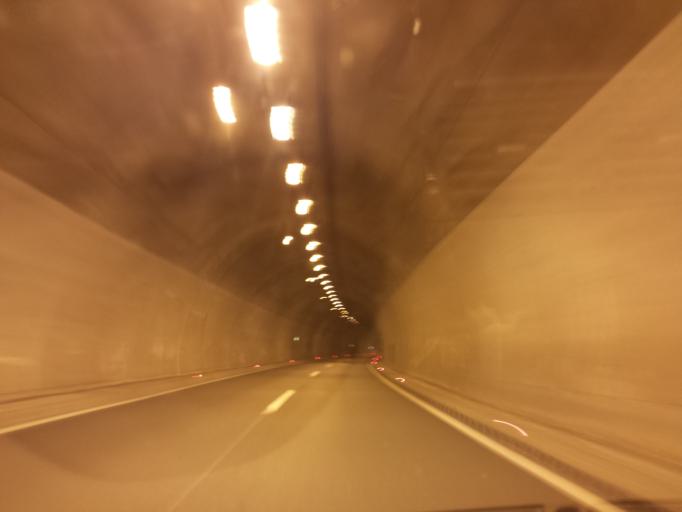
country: HR
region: Zadarska
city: Krusevo
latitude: 44.2603
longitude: 15.5993
